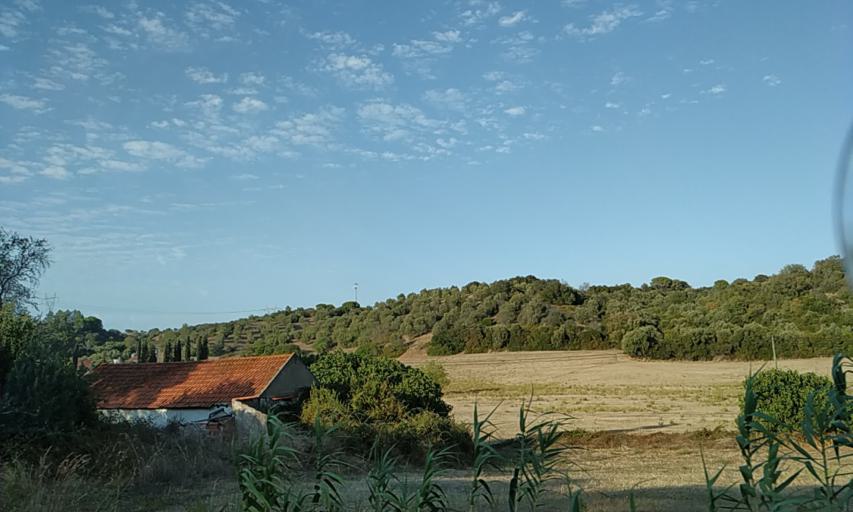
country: PT
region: Santarem
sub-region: Alcanena
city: Alcanena
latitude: 39.3678
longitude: -8.6575
